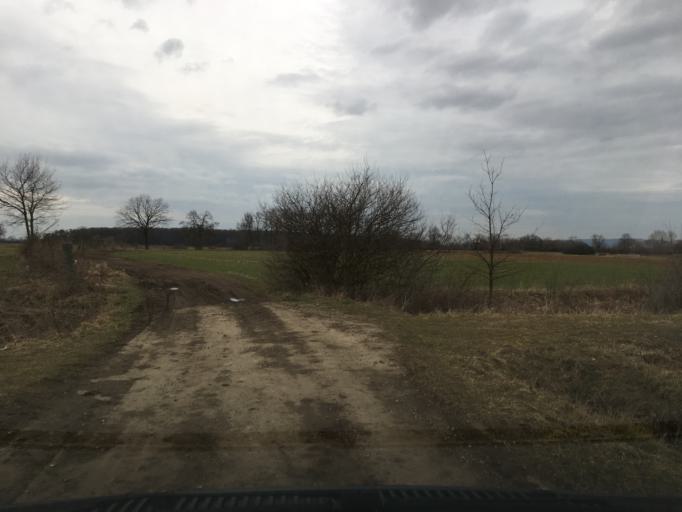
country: PL
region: Opole Voivodeship
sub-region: Powiat kedzierzynsko-kozielski
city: Wiekszyce
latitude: 50.3684
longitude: 18.1112
